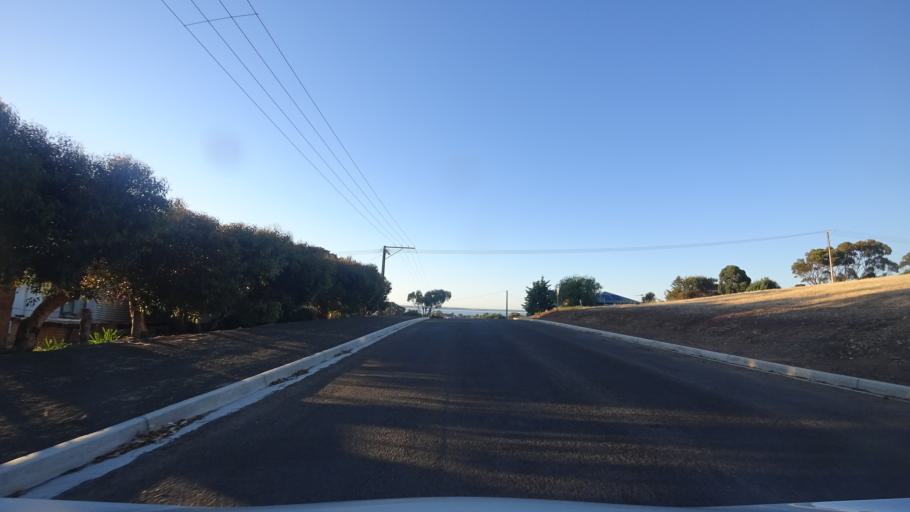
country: AU
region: South Australia
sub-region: Kangaroo Island
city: Kingscote
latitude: -35.6467
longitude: 137.6352
